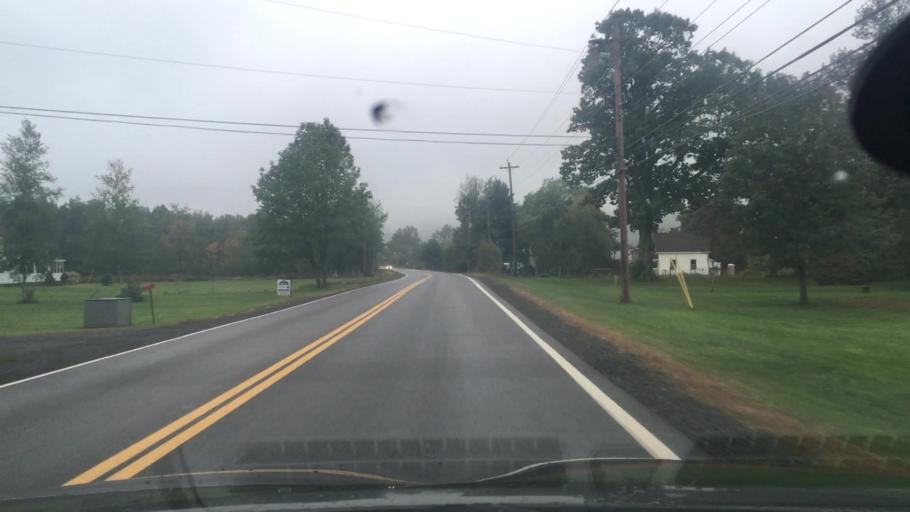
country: CA
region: Nova Scotia
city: Windsor
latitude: 44.9377
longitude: -64.1921
